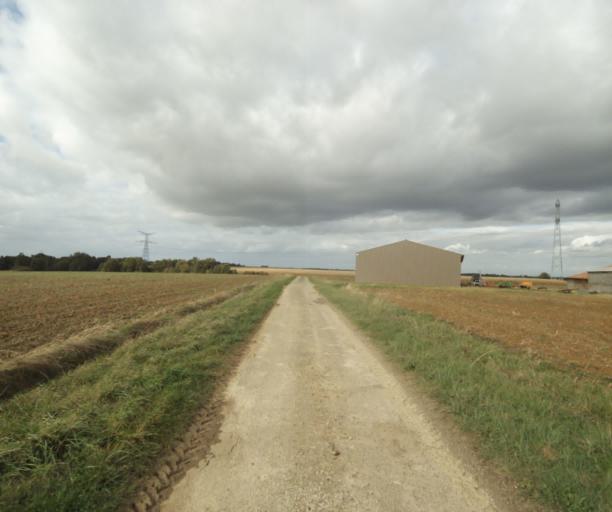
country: FR
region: Midi-Pyrenees
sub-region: Departement du Tarn-et-Garonne
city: Finhan
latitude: 43.9049
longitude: 1.1040
